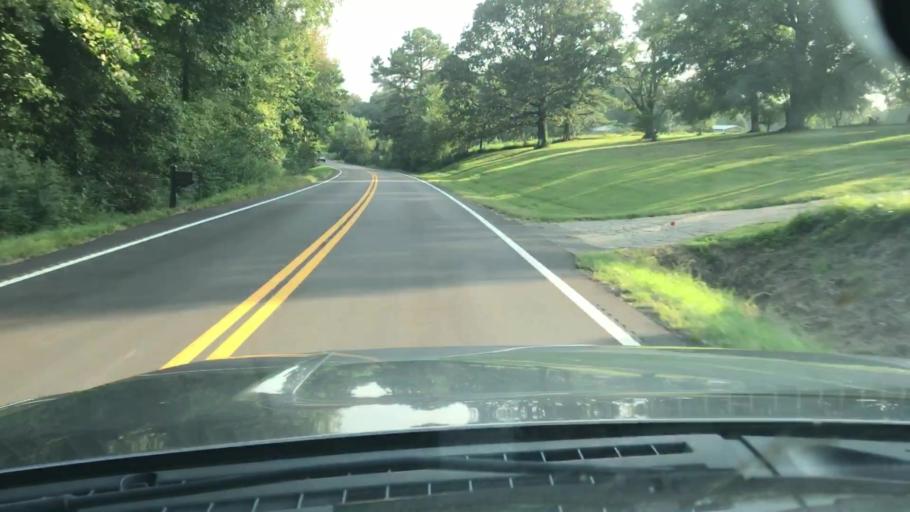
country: US
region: Tennessee
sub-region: Sumner County
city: Portland
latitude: 36.5625
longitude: -86.3877
